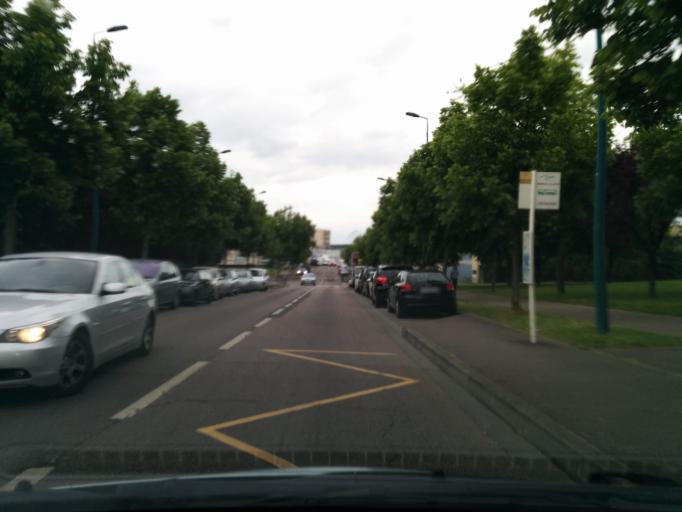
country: FR
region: Ile-de-France
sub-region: Departement des Yvelines
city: Buchelay
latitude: 48.9978
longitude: 1.6881
